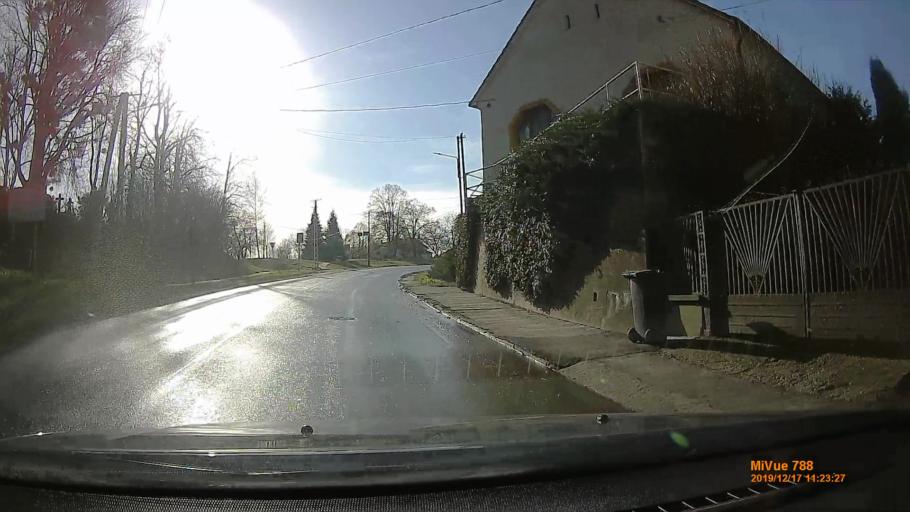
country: HU
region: Somogy
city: Kaposvar
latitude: 46.5052
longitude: 17.8187
